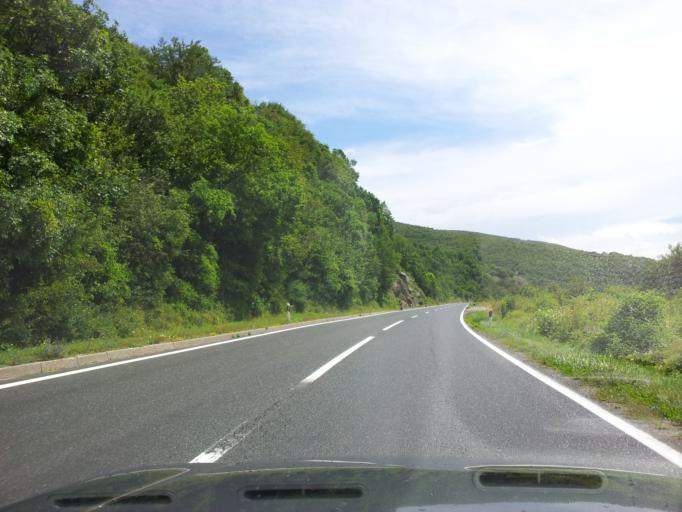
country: BA
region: Federation of Bosnia and Herzegovina
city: Bihac
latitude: 44.6167
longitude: 15.7386
